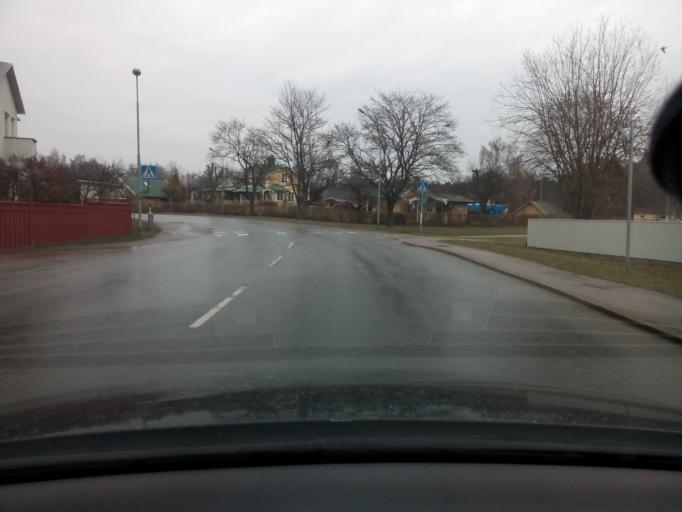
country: SE
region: Soedermanland
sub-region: Trosa Kommun
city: Trosa
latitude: 58.8928
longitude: 17.5539
